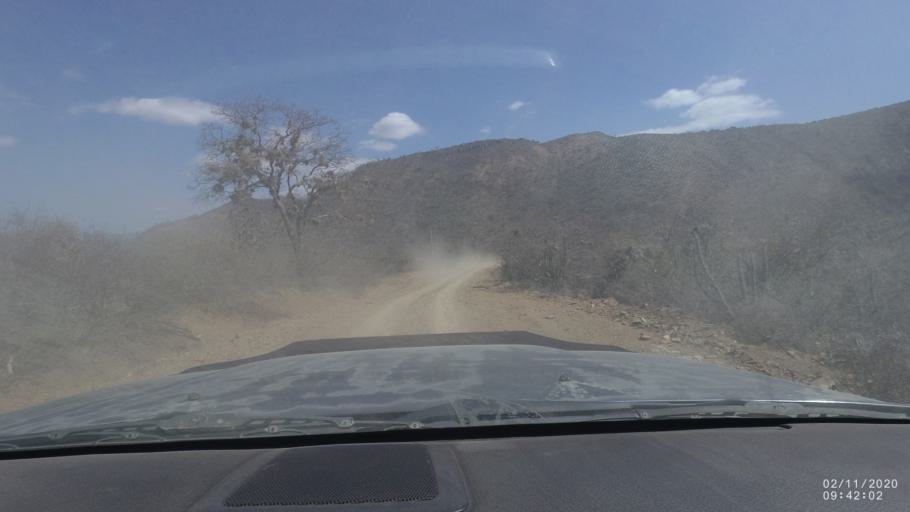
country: BO
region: Chuquisaca
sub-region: Provincia Zudanez
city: Mojocoya
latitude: -18.3939
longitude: -64.6032
